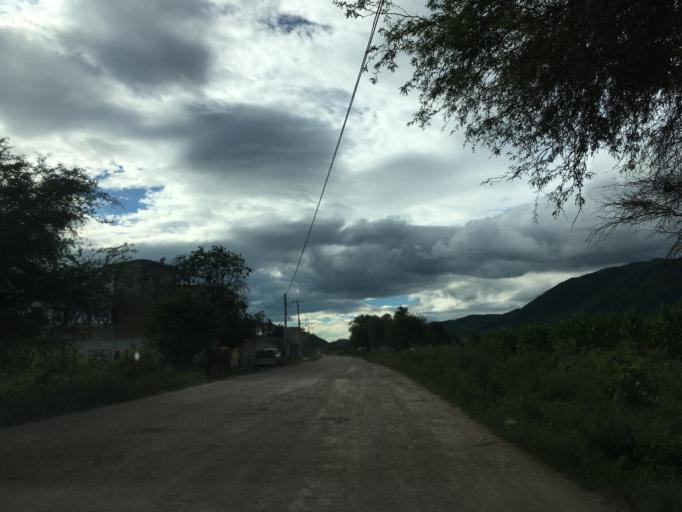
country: MX
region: Guanajuato
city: Iramuco
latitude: 19.9660
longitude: -100.9423
